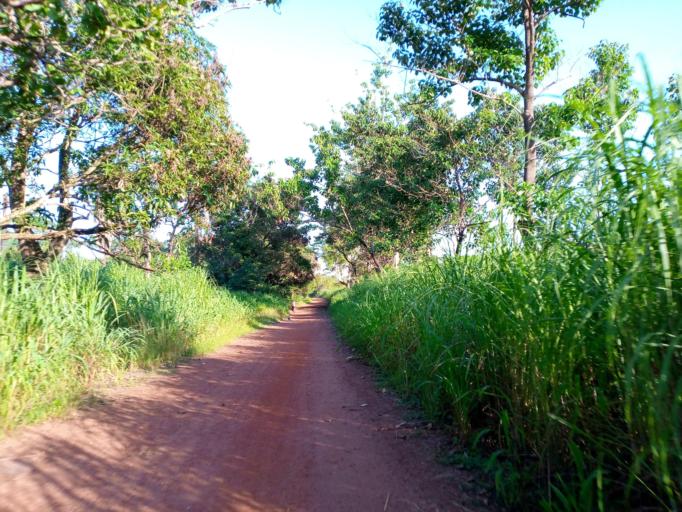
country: SL
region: Northern Province
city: Yonibana
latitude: 8.4522
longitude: -12.2449
